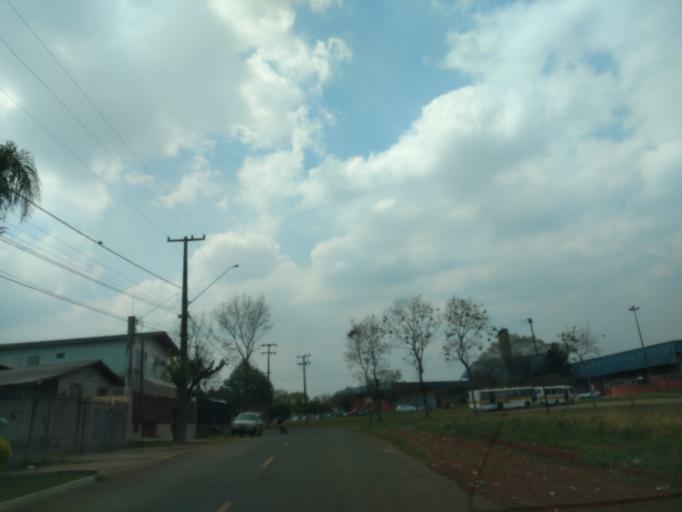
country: BR
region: Parana
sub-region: Guarapuava
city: Guarapuava
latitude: -25.3791
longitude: -51.4796
